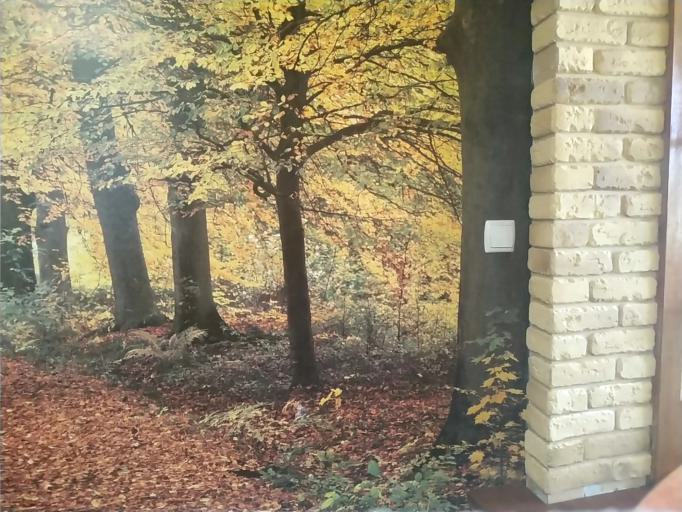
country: RU
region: Tverskaya
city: Vyshniy Volochek
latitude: 57.6925
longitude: 34.5044
